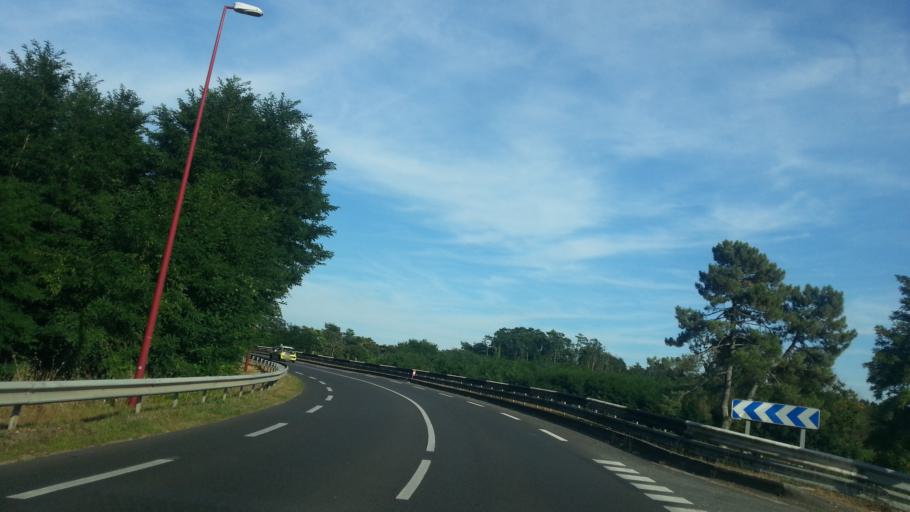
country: FR
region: Aquitaine
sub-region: Departement de la Gironde
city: Podensac
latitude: 44.6592
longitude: -0.3747
